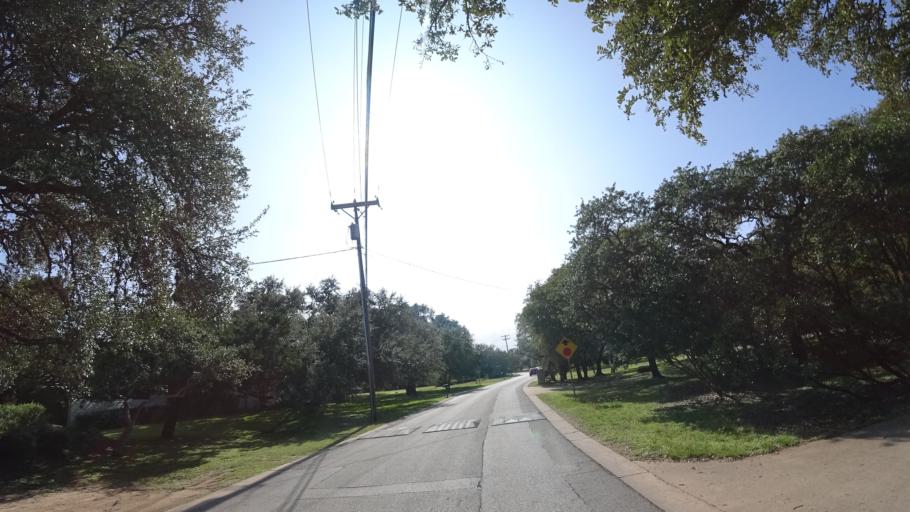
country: US
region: Texas
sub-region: Travis County
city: West Lake Hills
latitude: 30.2868
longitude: -97.8011
